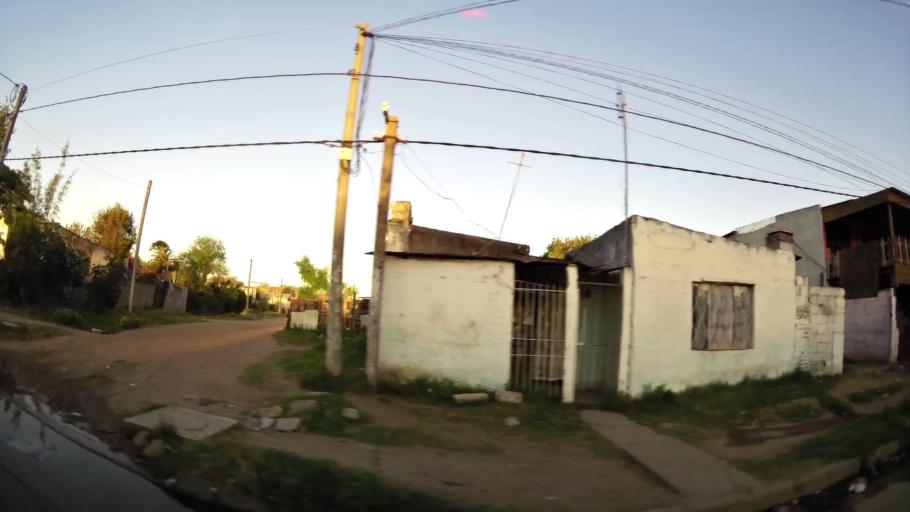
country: UY
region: Montevideo
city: Montevideo
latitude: -34.8334
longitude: -56.1555
